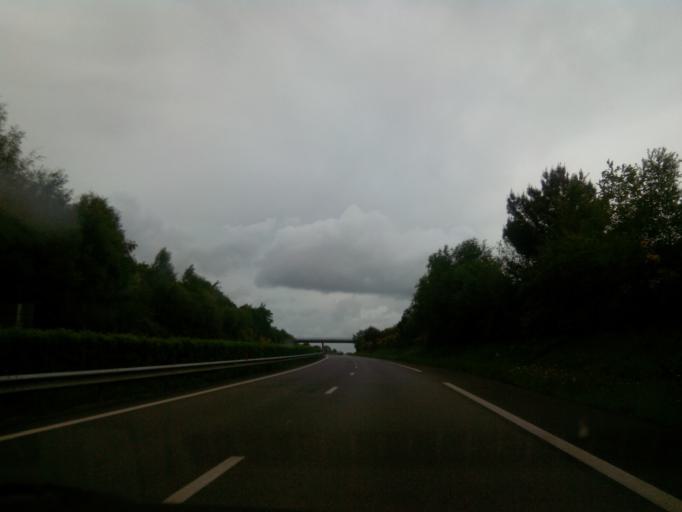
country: FR
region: Brittany
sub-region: Departement du Morbihan
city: Trefflean
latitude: 47.7028
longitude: -2.6191
